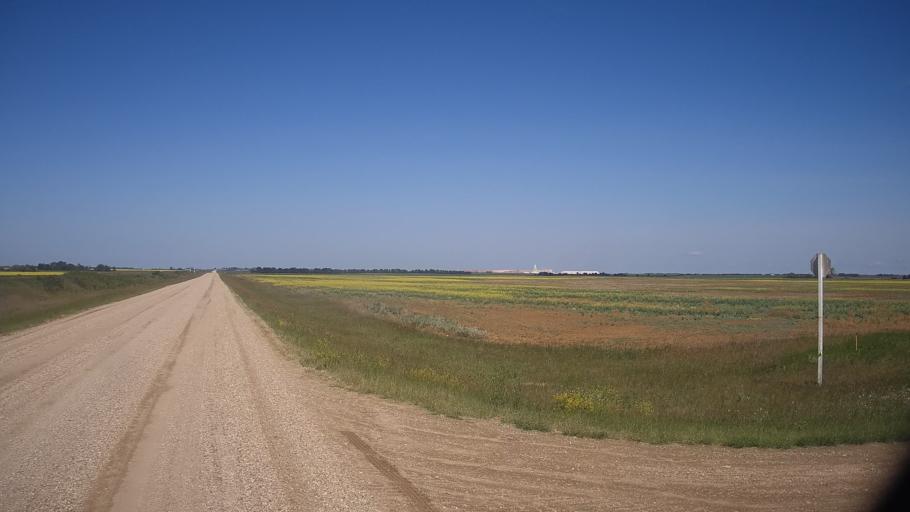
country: CA
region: Saskatchewan
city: Watrous
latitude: 51.8717
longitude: -105.9952
